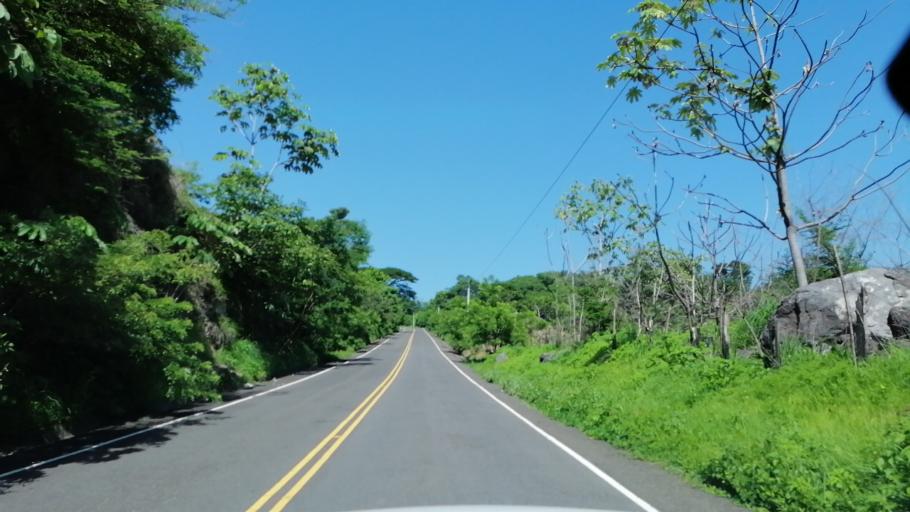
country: HN
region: Lempira
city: La Virtud
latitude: 13.9785
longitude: -88.7601
